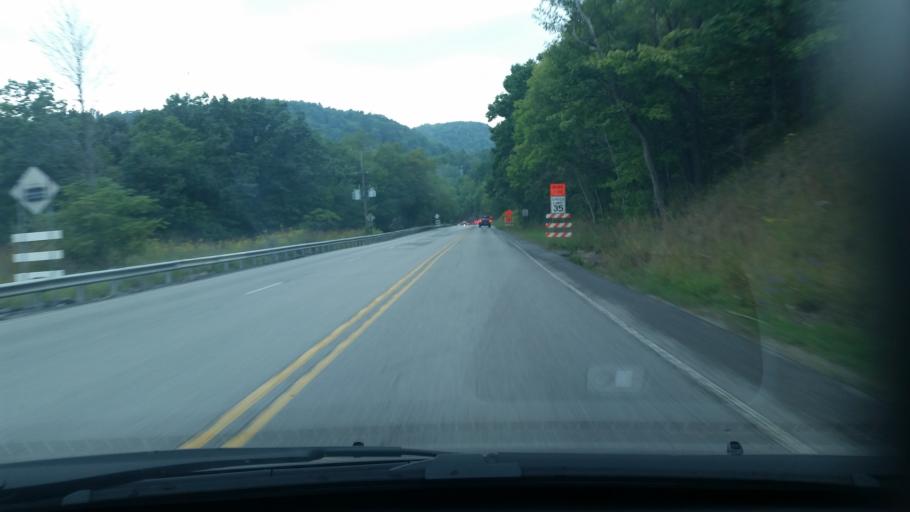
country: US
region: Pennsylvania
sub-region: Clearfield County
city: Shiloh
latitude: 41.0664
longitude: -78.3542
